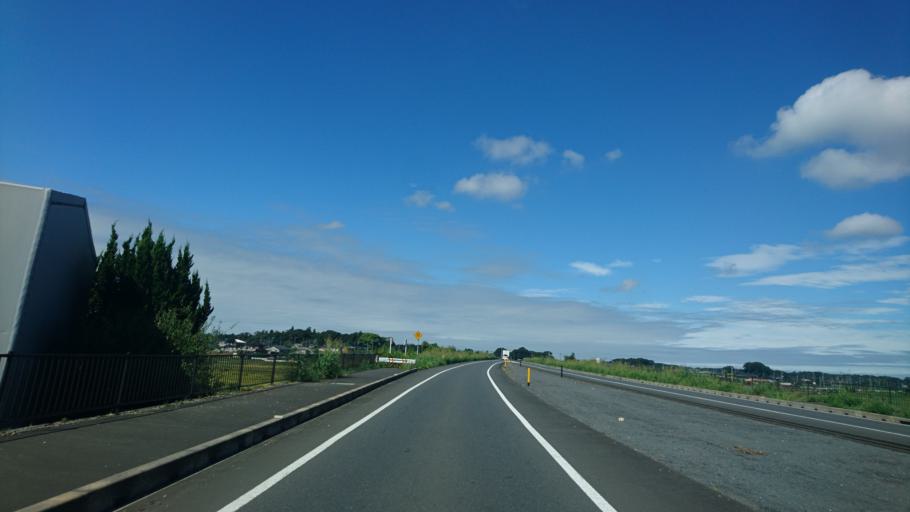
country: JP
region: Ibaraki
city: Iwai
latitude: 36.0623
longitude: 139.9031
